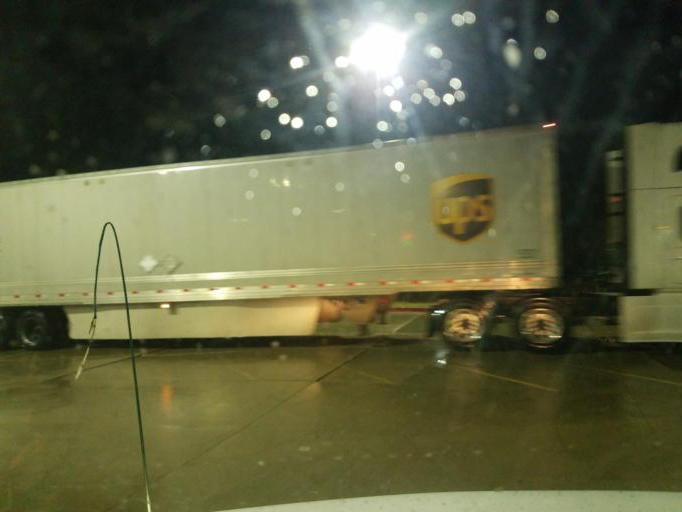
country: US
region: Illinois
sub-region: Clark County
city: Marshall
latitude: 39.4254
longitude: -87.6919
